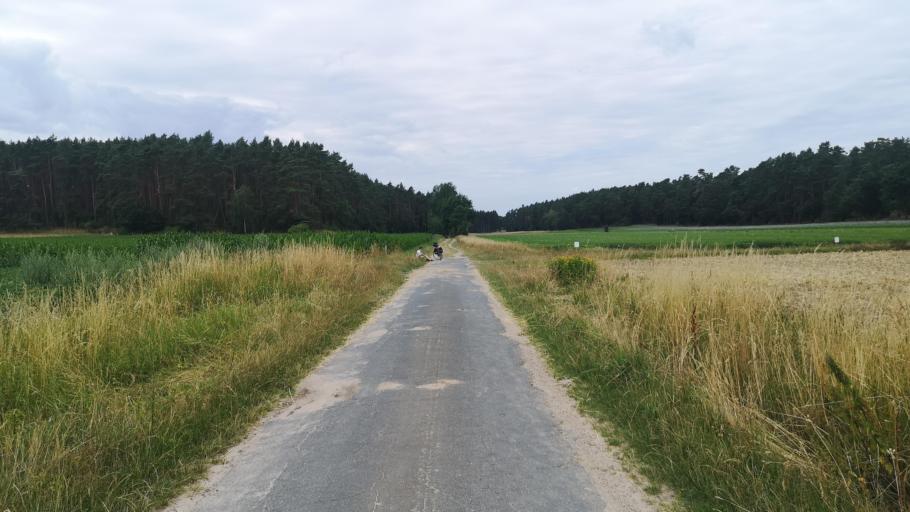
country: DE
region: Lower Saxony
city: Dahlem
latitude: 53.2165
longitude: 10.7457
